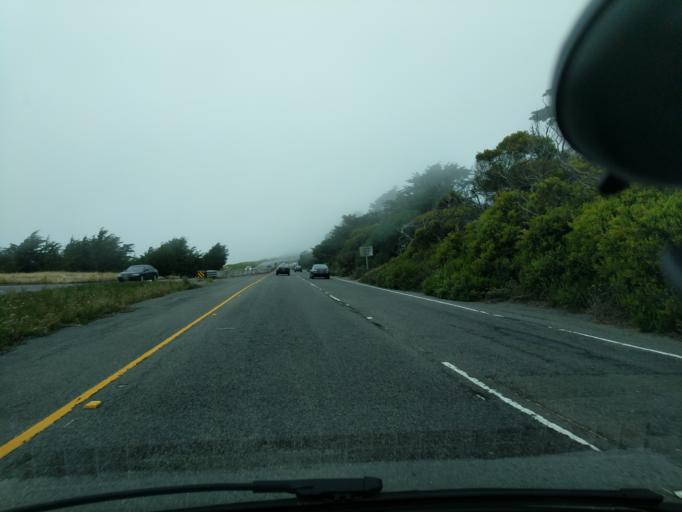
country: US
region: California
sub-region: San Mateo County
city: Broadmoor
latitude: 37.7029
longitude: -122.4970
